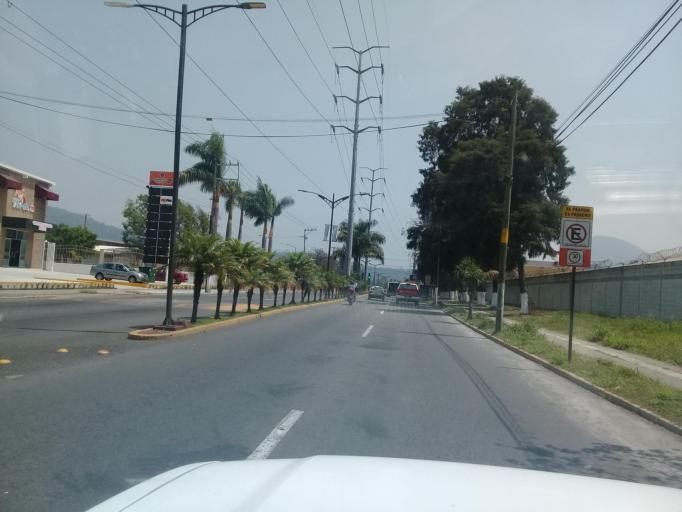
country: MX
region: Veracruz
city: Ixtac Zoquitlan
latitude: 18.8611
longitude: -97.0584
